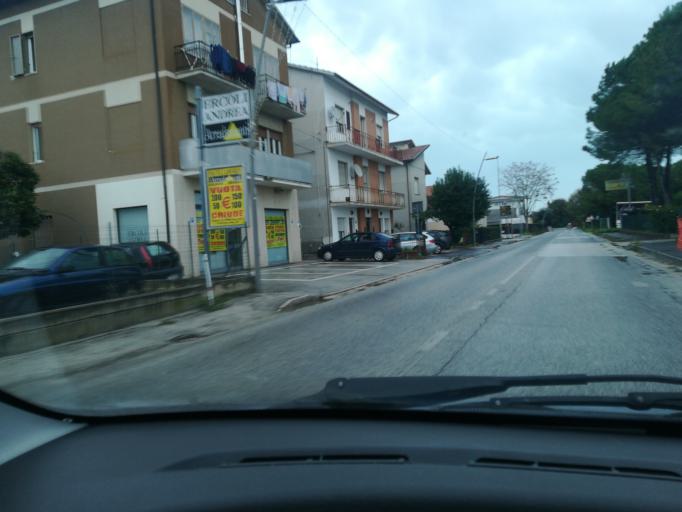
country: IT
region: The Marches
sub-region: Provincia di Macerata
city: Trodica
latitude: 43.2753
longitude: 13.5979
